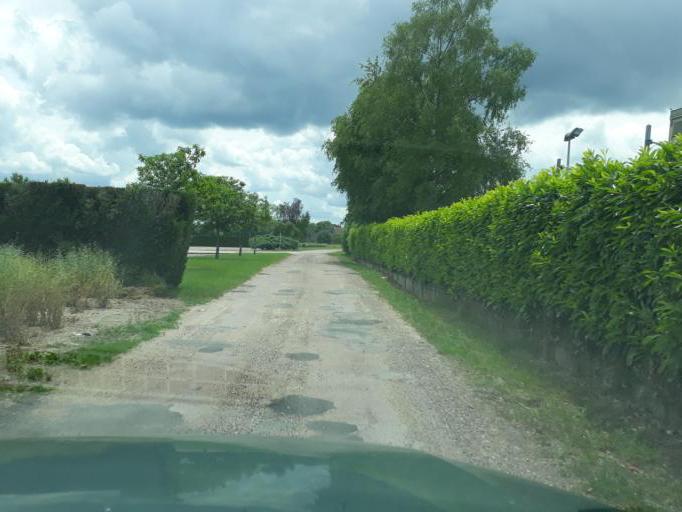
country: FR
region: Centre
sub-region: Departement du Loiret
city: Mareau-aux-Pres
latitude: 47.8817
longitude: 1.8044
